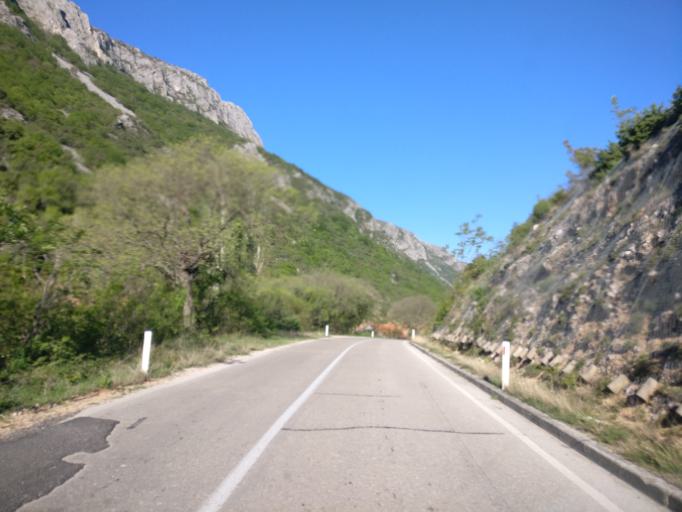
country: BA
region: Federation of Bosnia and Herzegovina
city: Stolac
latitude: 43.0737
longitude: 18.0319
